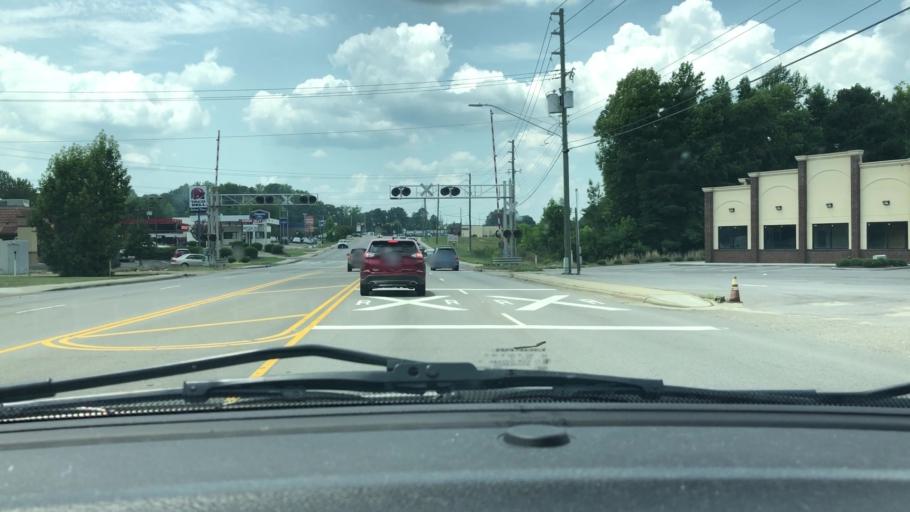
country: US
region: North Carolina
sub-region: Lee County
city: Sanford
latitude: 35.4615
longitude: -79.1559
